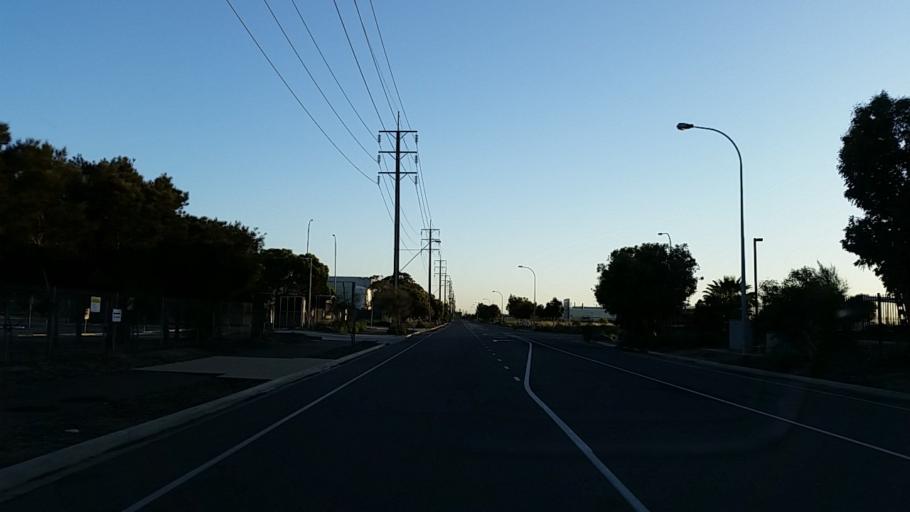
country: AU
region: South Australia
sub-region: Port Adelaide Enfield
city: Birkenhead
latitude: -34.7807
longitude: 138.5084
